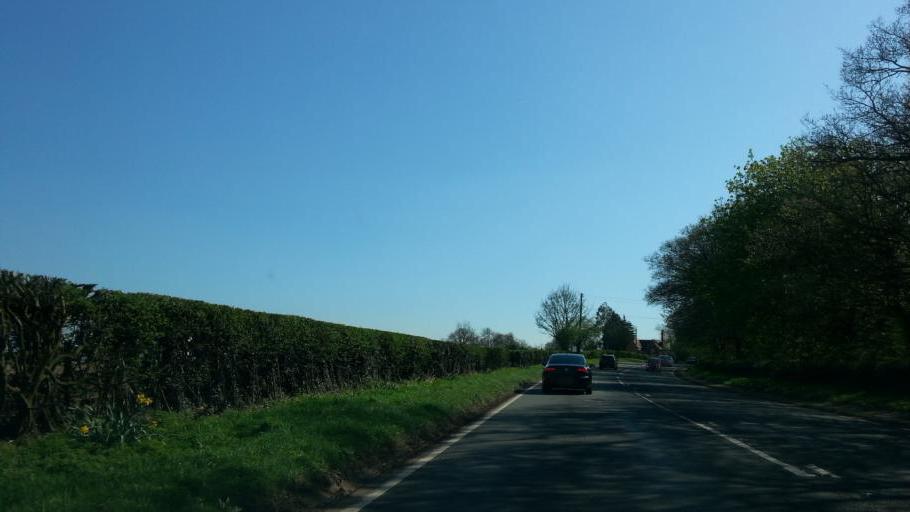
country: GB
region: England
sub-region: Worcestershire
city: Alvechurch
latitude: 52.3845
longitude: -1.9577
